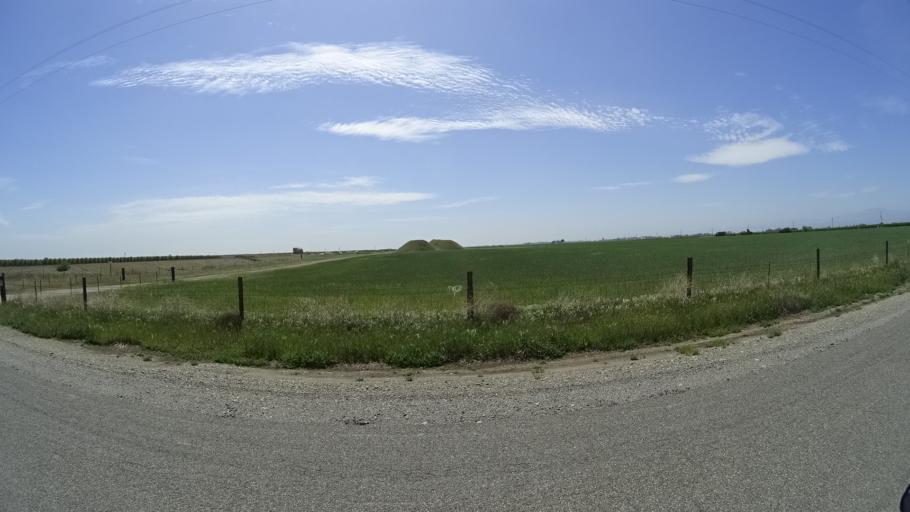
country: US
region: California
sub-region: Glenn County
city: Orland
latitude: 39.6531
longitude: -122.1742
